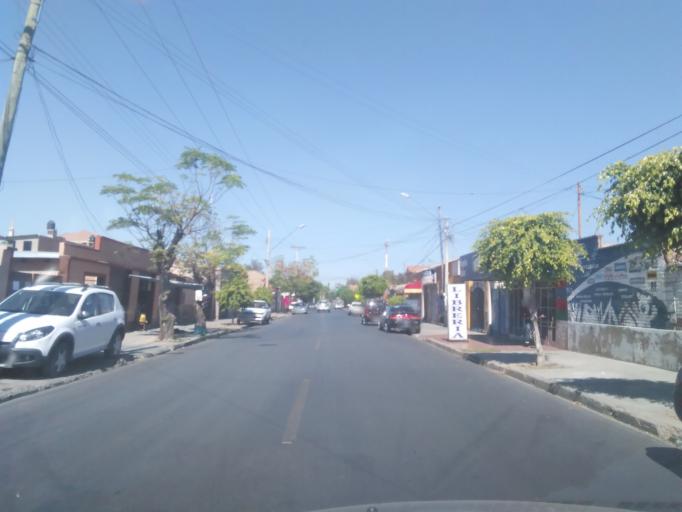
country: BO
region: Cochabamba
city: Cochabamba
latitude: -17.3967
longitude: -66.1406
